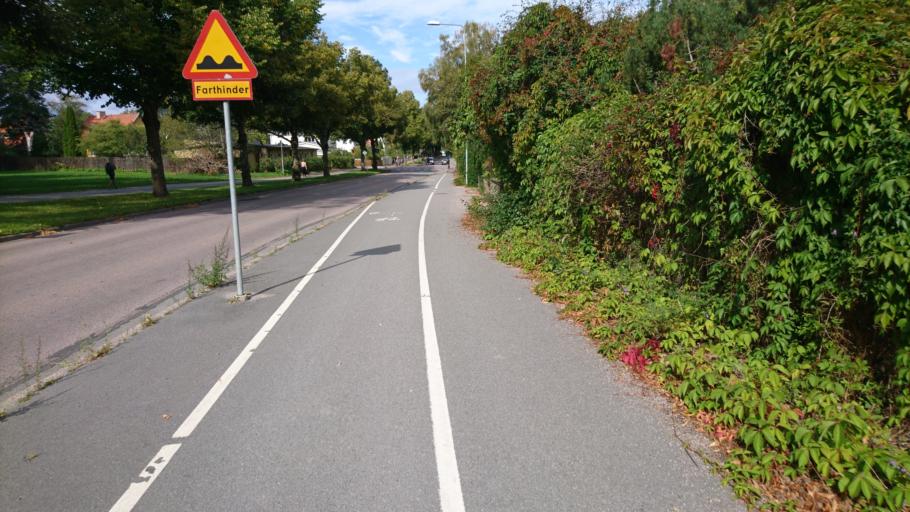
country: SE
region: Uppsala
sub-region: Uppsala Kommun
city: Uppsala
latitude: 59.8472
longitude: 17.6236
